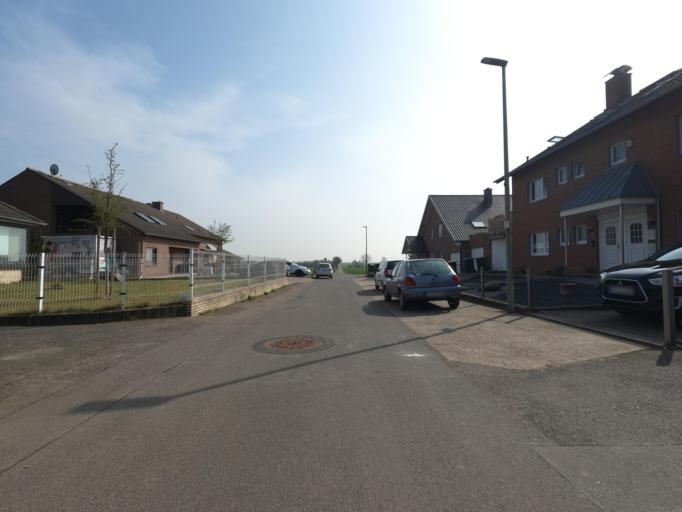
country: DE
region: North Rhine-Westphalia
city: Erkelenz
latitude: 51.0586
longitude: 6.3534
